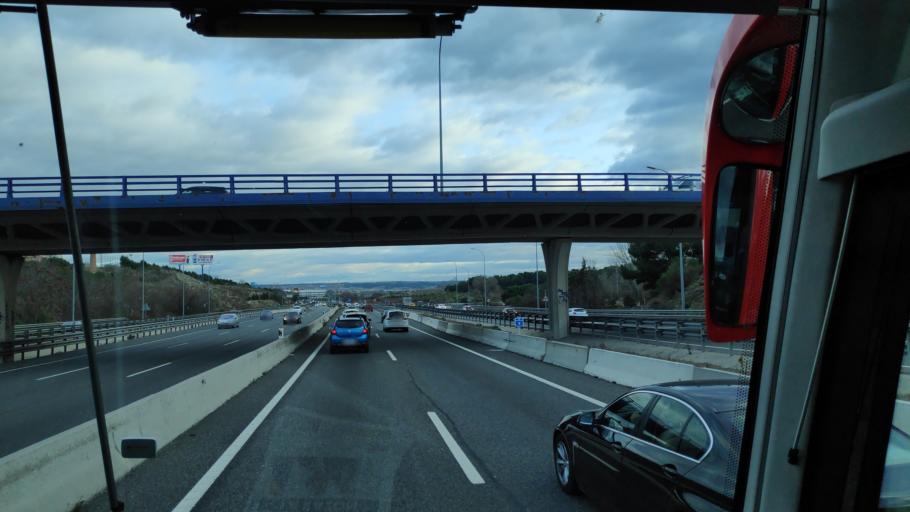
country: ES
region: Madrid
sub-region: Provincia de Madrid
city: Vaciamadrid
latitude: 40.3537
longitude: -3.5522
